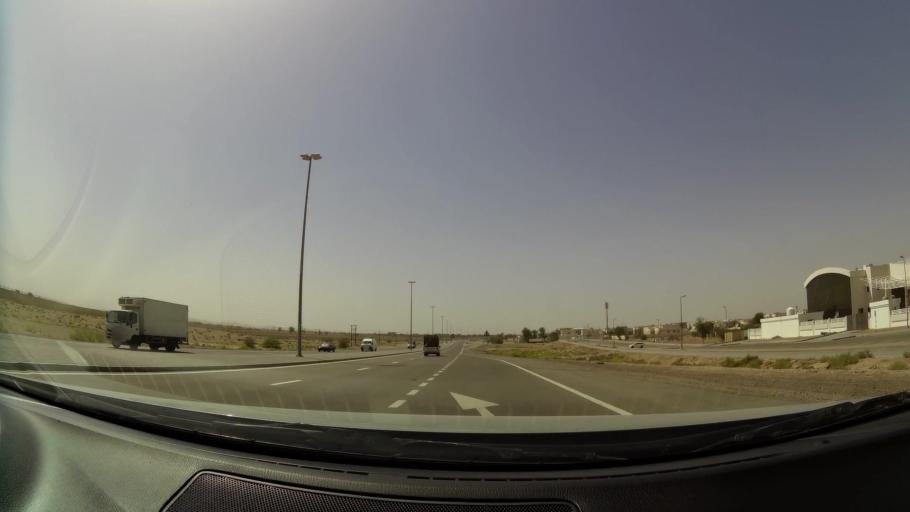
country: OM
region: Al Buraimi
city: Al Buraymi
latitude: 24.3124
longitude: 55.7573
